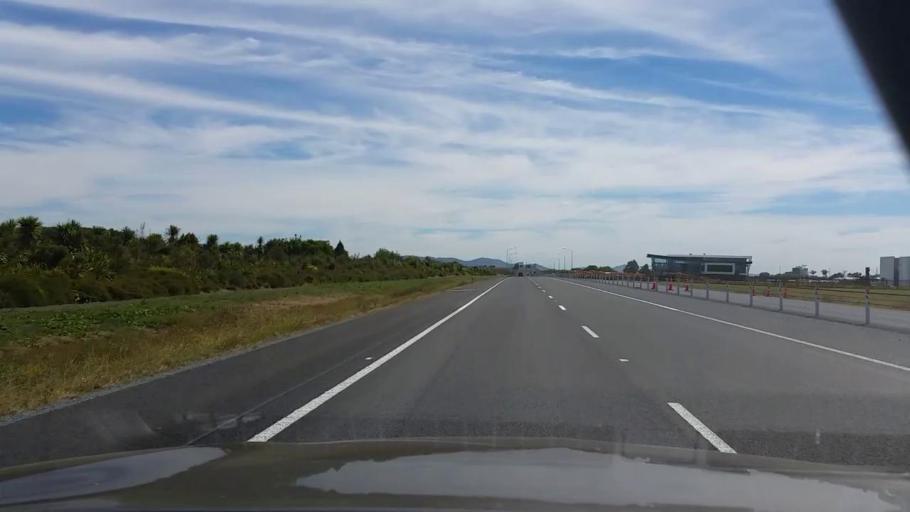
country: NZ
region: Waikato
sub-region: Hamilton City
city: Hamilton
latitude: -37.7433
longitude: 175.2138
